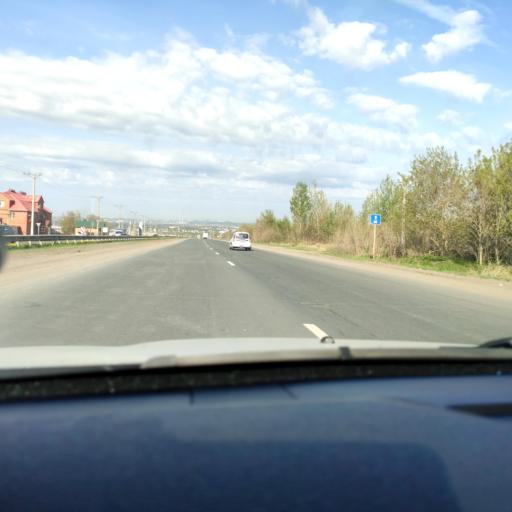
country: RU
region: Samara
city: Smyshlyayevka
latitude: 53.2582
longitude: 50.4403
